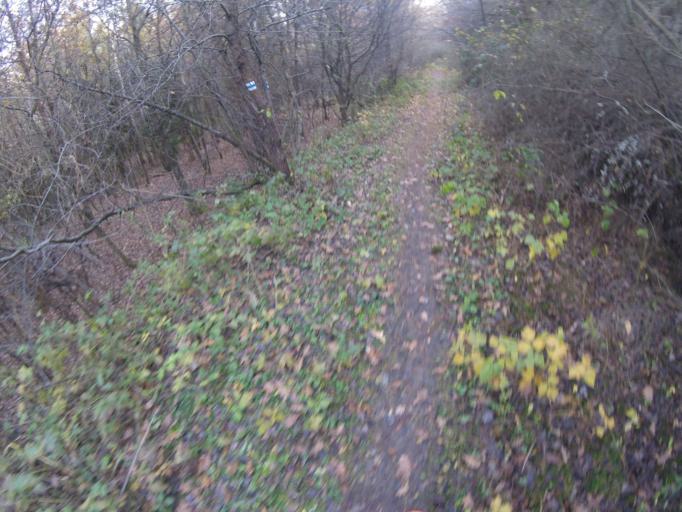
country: HU
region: Borsod-Abauj-Zemplen
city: Gonc
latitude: 48.4861
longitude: 21.4691
